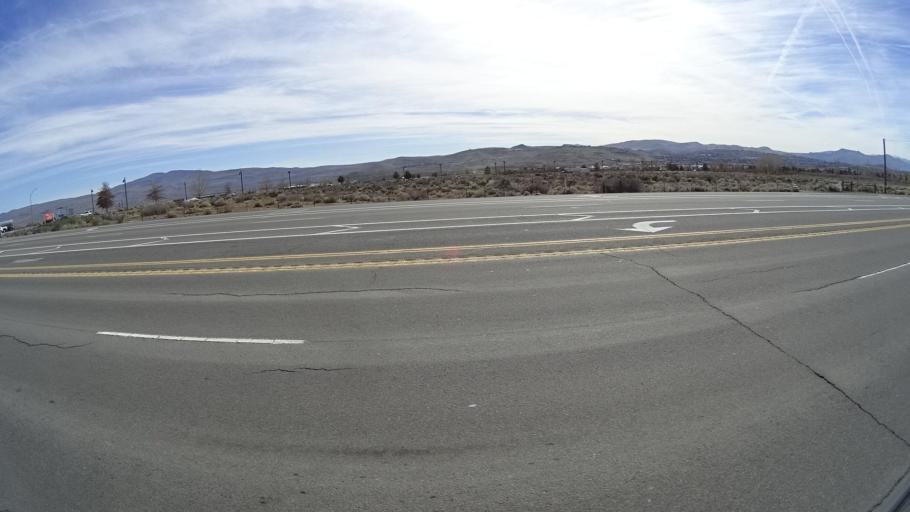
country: US
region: Nevada
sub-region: Washoe County
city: Sun Valley
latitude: 39.6078
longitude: -119.7328
